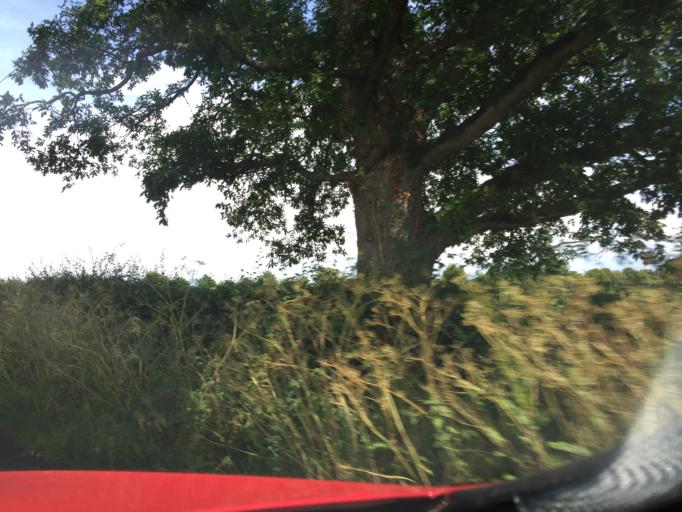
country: GB
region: England
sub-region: Gloucestershire
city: Tetbury
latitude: 51.6329
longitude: -2.1875
